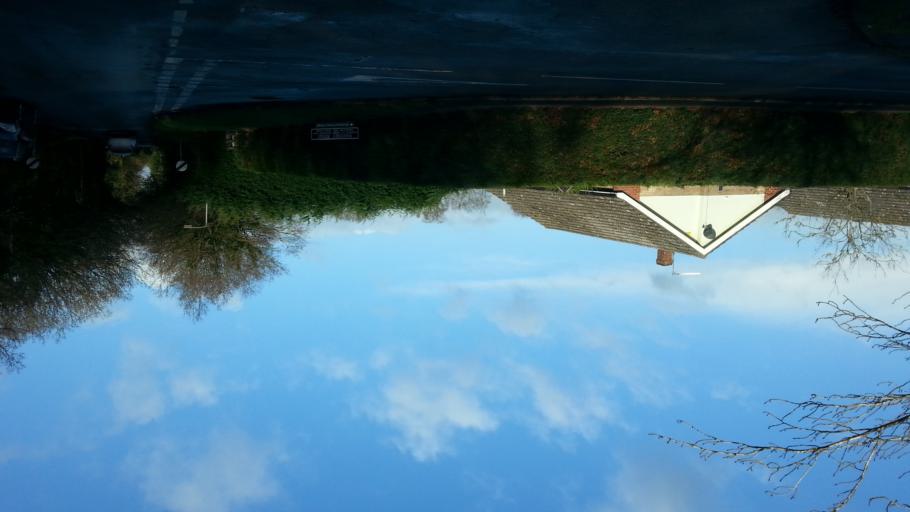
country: GB
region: England
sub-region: Norfolk
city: Ditchingham
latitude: 52.4712
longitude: 1.4510
